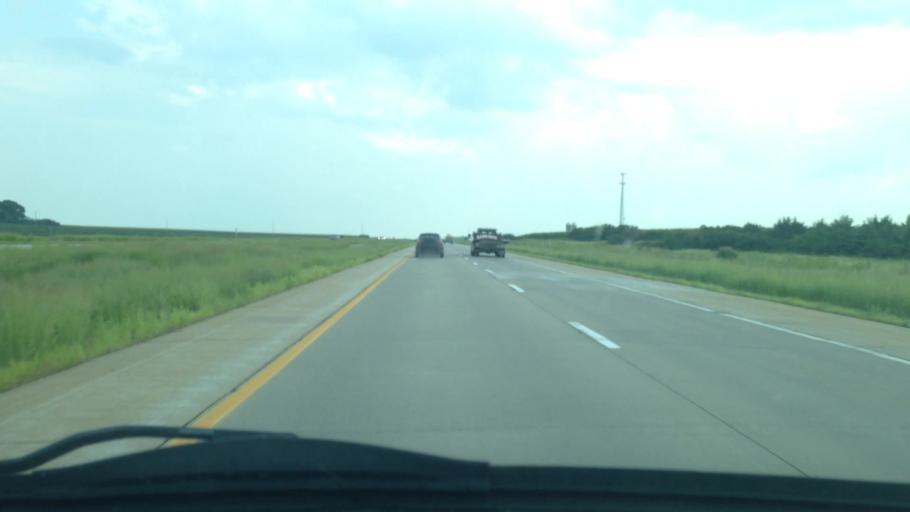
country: US
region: Iowa
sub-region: Black Hawk County
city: La Porte City
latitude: 42.3936
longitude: -92.1403
